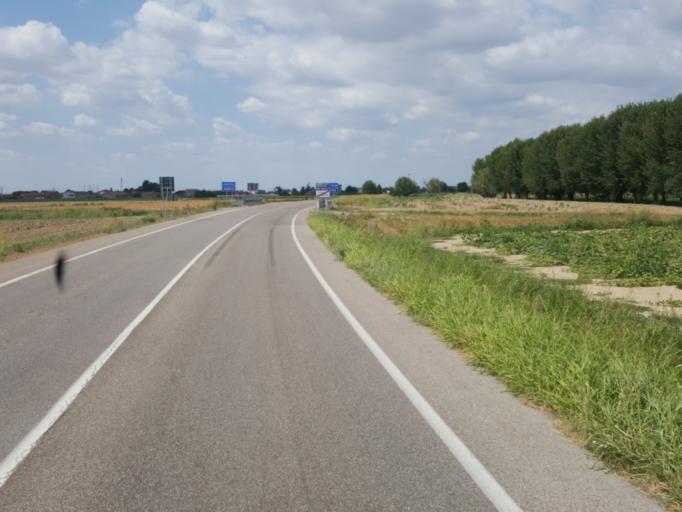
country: IT
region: Veneto
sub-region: Provincia di Rovigo
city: Melara
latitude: 45.0799
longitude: 11.1853
